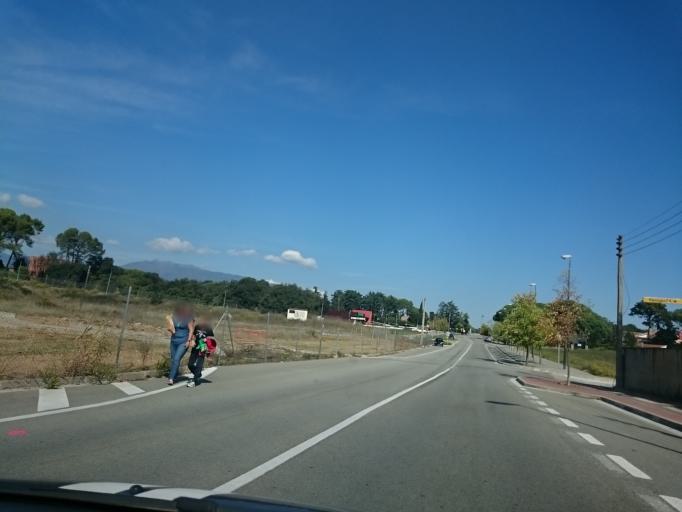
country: ES
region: Catalonia
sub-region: Provincia de Barcelona
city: Llinars del Valles
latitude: 41.6422
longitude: 2.4076
